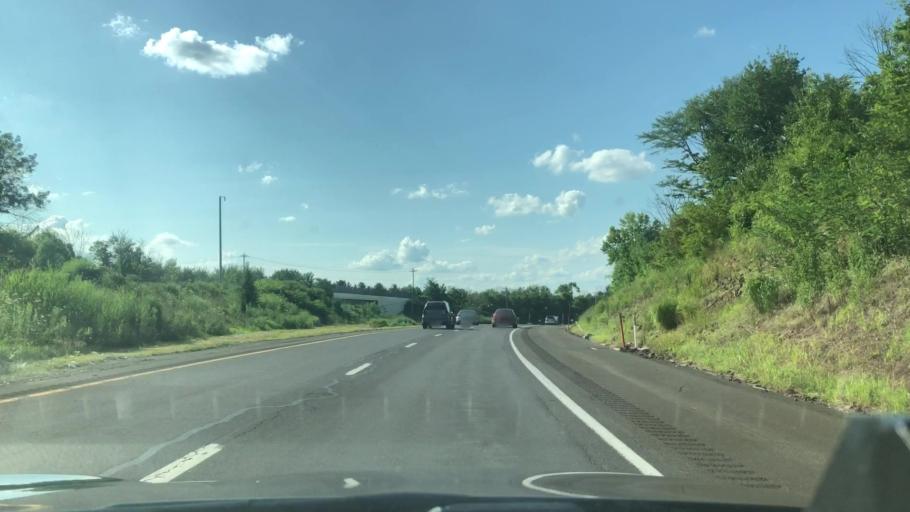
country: US
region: Pennsylvania
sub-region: Montgomery County
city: Spring House
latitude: 40.1950
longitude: -75.2221
